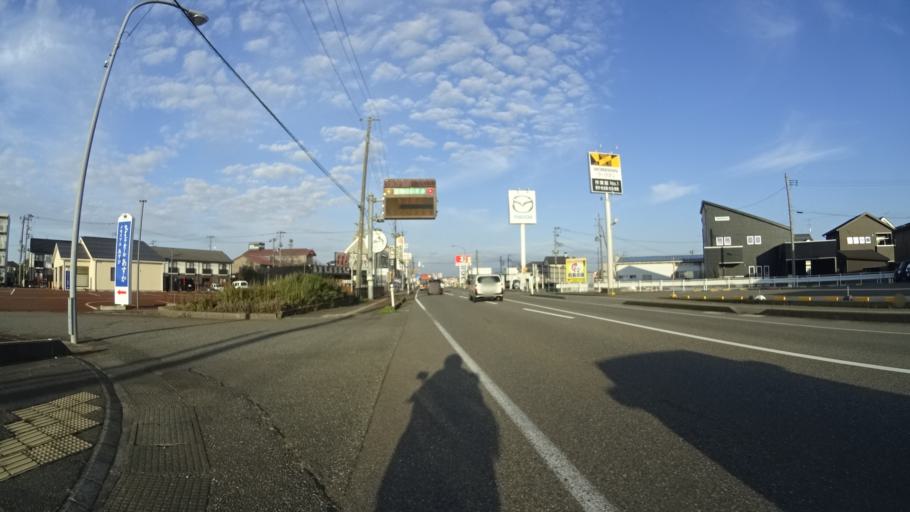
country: JP
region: Niigata
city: Kashiwazaki
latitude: 37.3653
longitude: 138.5719
